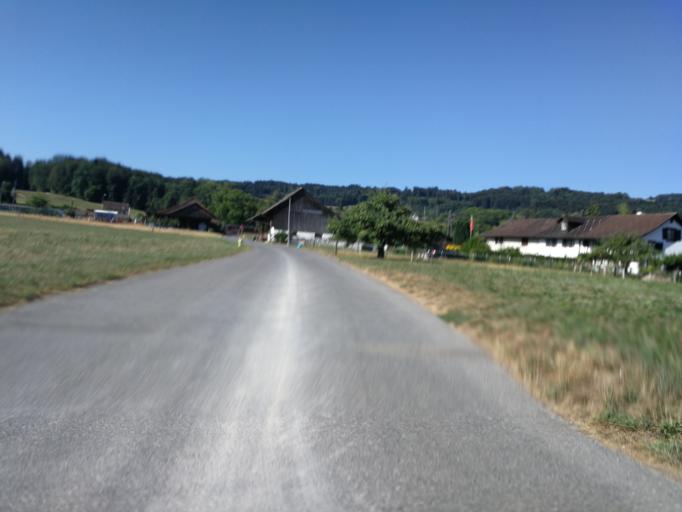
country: CH
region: Zurich
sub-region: Bezirk Uster
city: Esslingen
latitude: 47.2939
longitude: 8.7038
